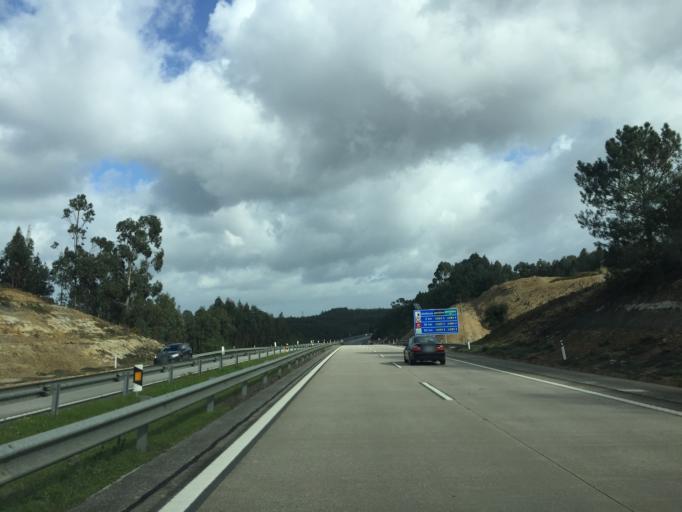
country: PT
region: Lisbon
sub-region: Torres Vedras
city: A dos Cunhados
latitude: 39.1447
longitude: -9.2452
